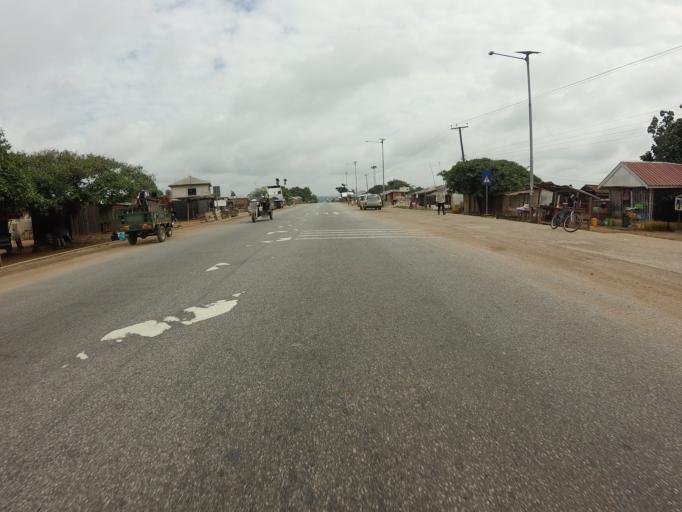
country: GH
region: Ashanti
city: Tafo
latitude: 6.9935
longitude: -1.6948
